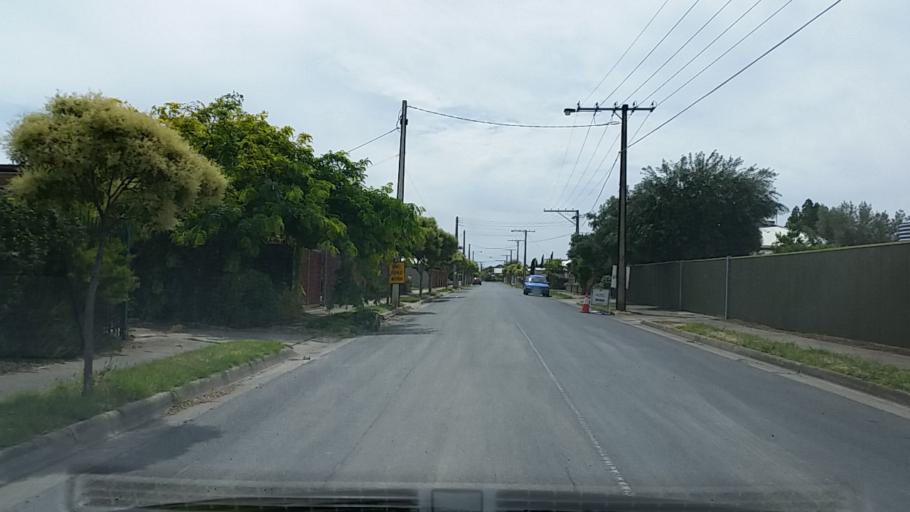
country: AU
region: South Australia
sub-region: Charles Sturt
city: Woodville
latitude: -34.8825
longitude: 138.5560
